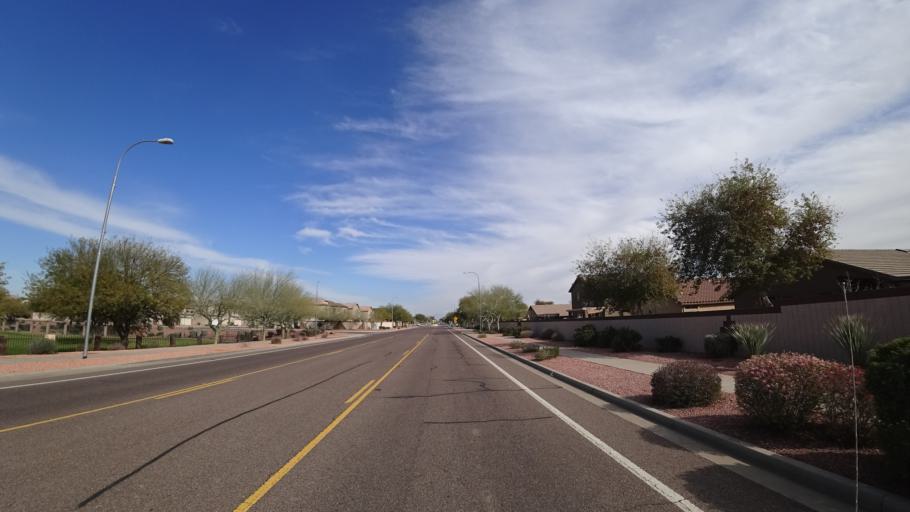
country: US
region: Arizona
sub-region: Maricopa County
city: Avondale
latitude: 33.4281
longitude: -112.3049
